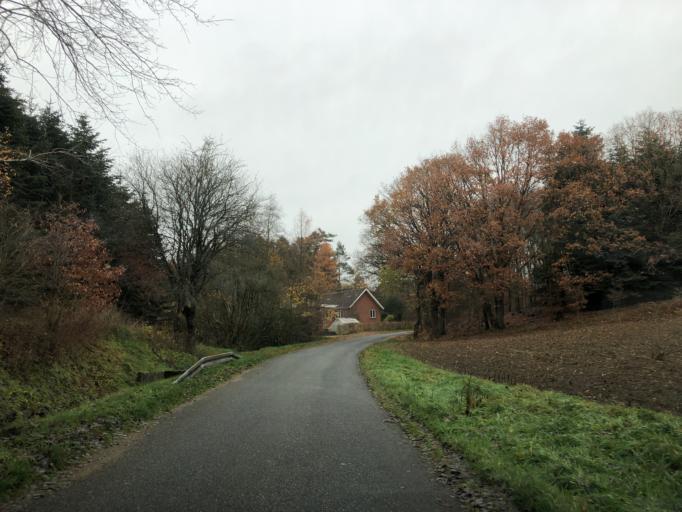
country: DK
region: Central Jutland
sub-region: Silkeborg Kommune
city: Svejbaek
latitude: 56.0967
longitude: 9.6071
